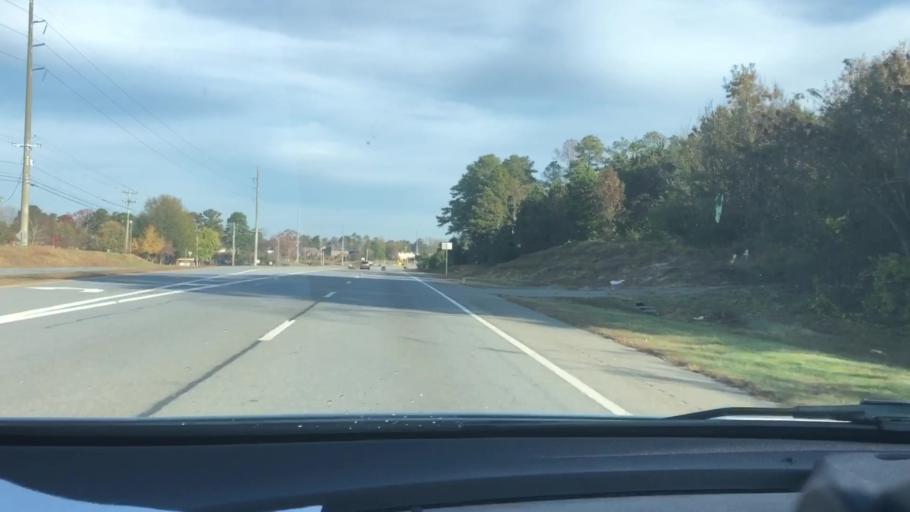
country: US
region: Georgia
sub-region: Fulton County
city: Johns Creek
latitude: 34.1108
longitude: -84.1765
